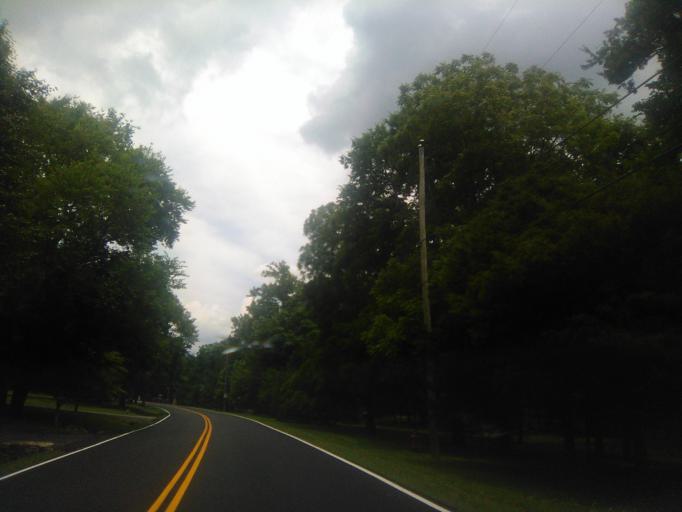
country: US
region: Tennessee
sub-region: Davidson County
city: Forest Hills
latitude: 36.0738
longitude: -86.8655
